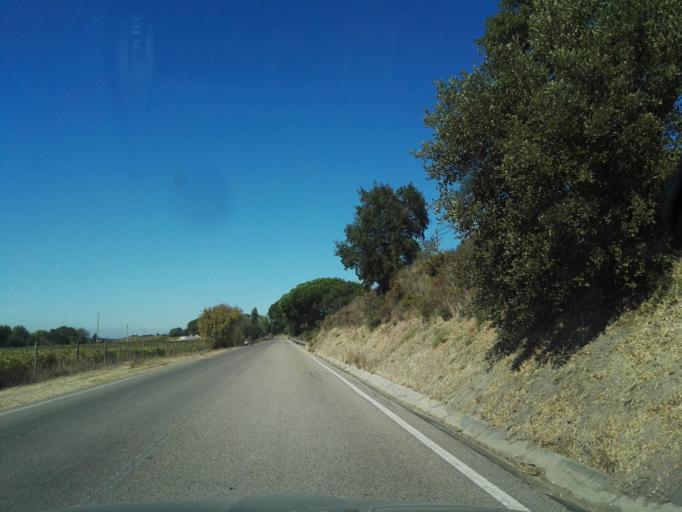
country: PT
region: Santarem
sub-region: Benavente
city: Poceirao
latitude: 38.8526
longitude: -8.7232
